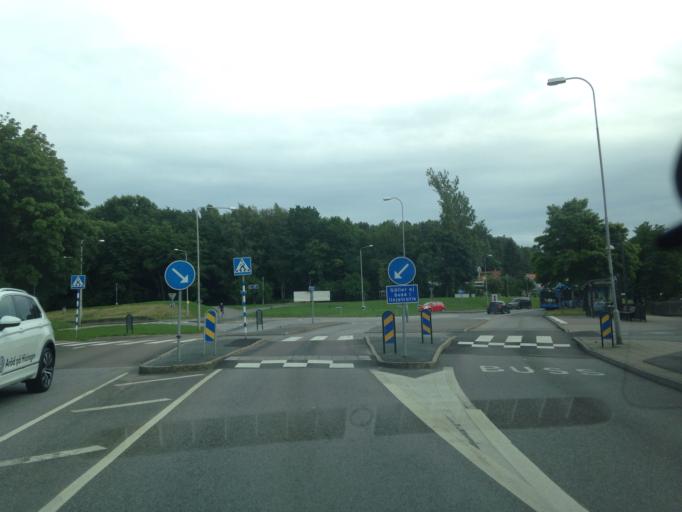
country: SE
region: Vaestra Goetaland
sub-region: Goteborg
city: Goeteborg
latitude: 57.7320
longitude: 11.9751
